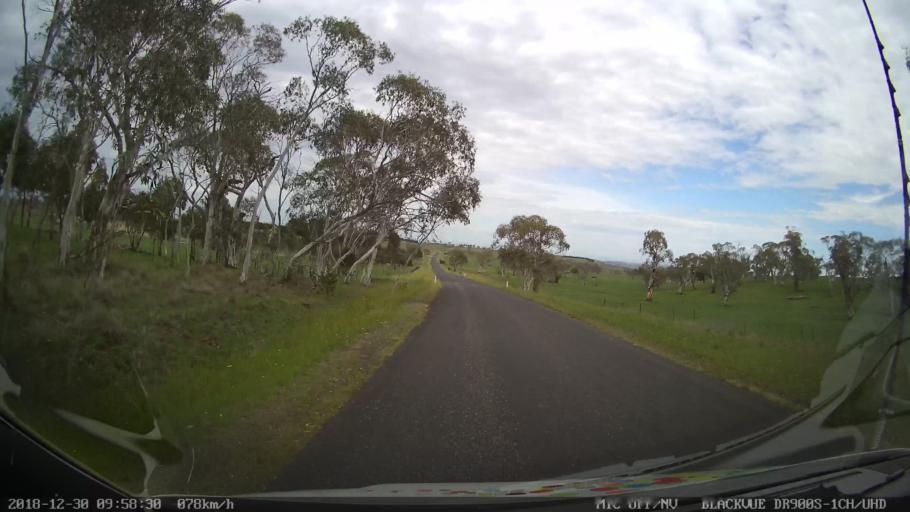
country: AU
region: New South Wales
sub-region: Cooma-Monaro
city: Cooma
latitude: -36.5221
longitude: 149.2253
